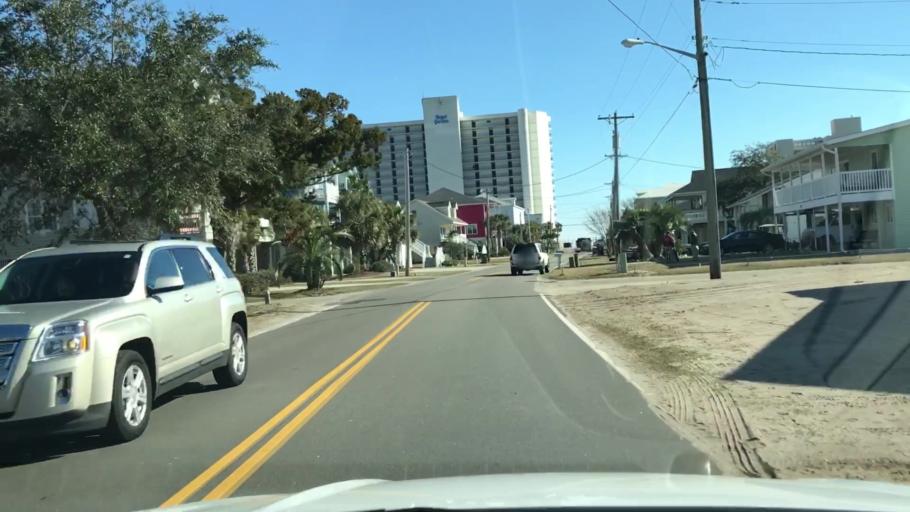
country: US
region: South Carolina
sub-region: Horry County
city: Garden City
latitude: 33.5869
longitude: -78.9927
